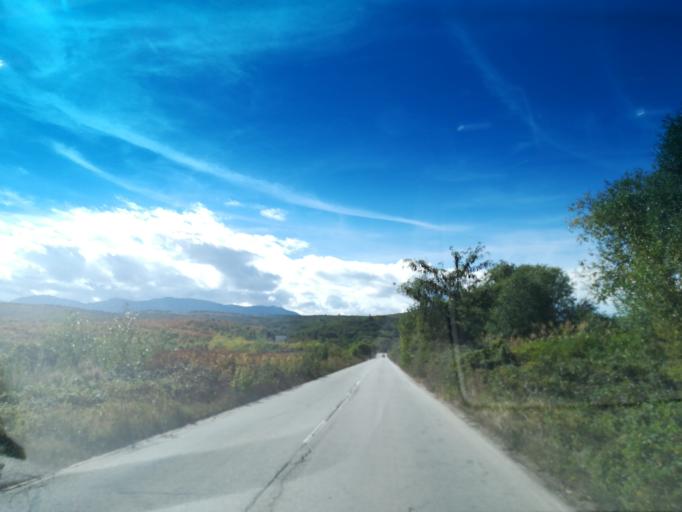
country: BG
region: Plovdiv
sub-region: Obshtina Krichim
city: Krichim
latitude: 42.0728
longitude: 24.4067
